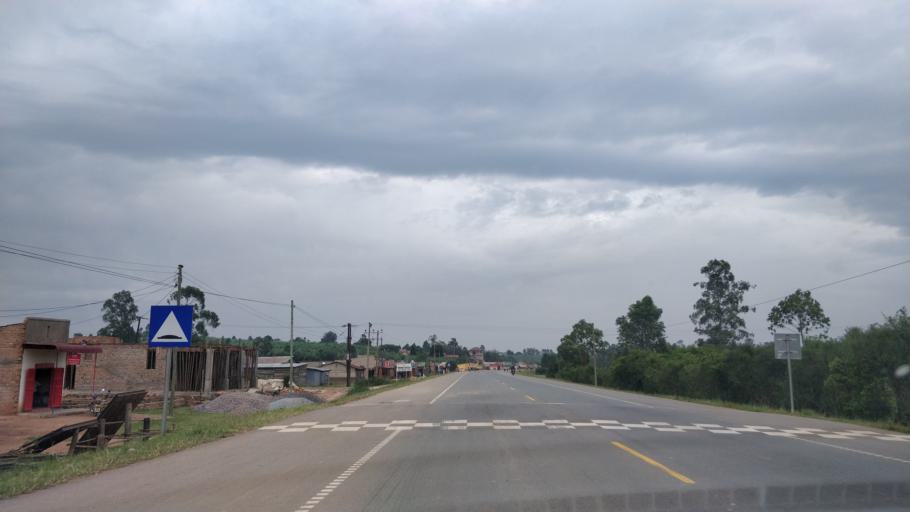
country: UG
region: Western Region
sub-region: Sheema District
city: Kibingo
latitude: -0.6623
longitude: 30.4532
